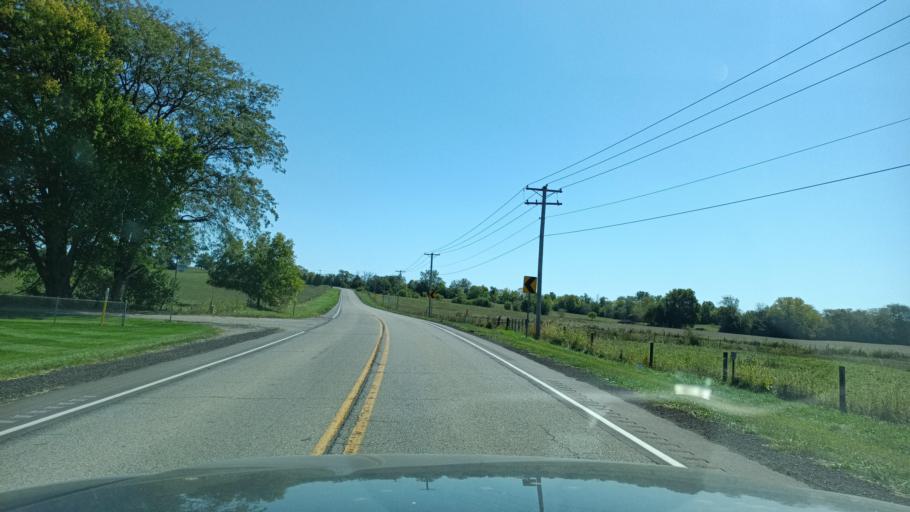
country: US
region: Illinois
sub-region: Woodford County
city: Eureka
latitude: 40.6211
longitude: -89.2400
